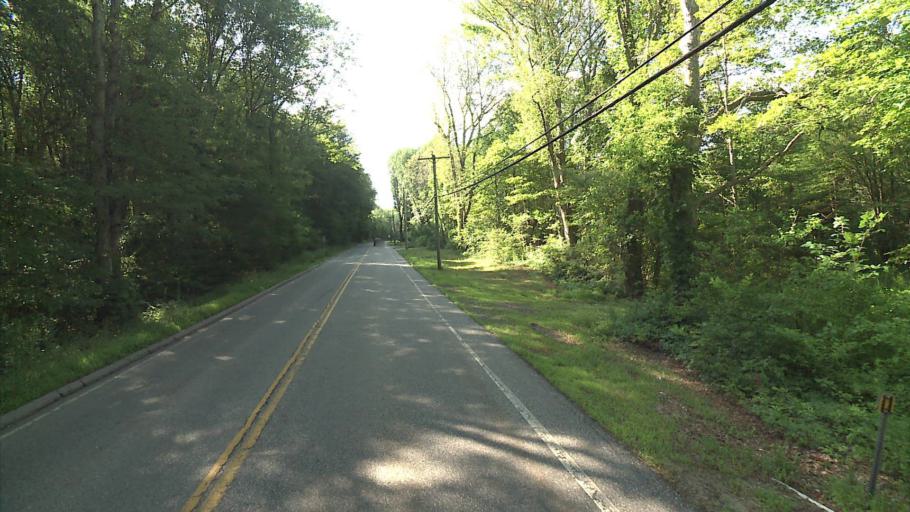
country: US
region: Connecticut
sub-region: New London County
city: Montville Center
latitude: 41.5008
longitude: -72.2001
